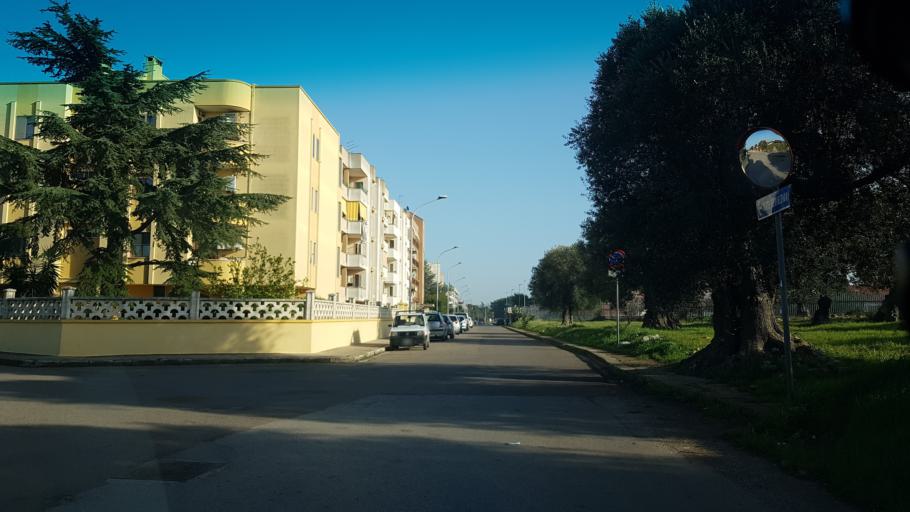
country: IT
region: Apulia
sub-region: Provincia di Brindisi
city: San Vito dei Normanni
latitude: 40.6641
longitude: 17.6934
